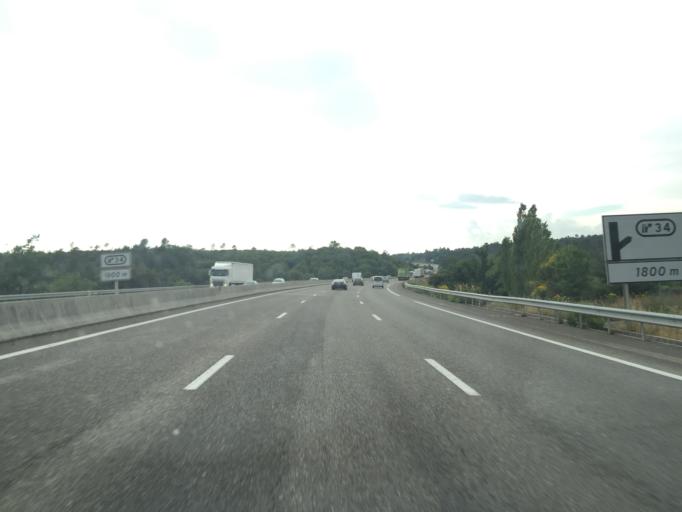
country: FR
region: Provence-Alpes-Cote d'Azur
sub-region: Departement du Var
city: Tourves
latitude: 43.4384
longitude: 5.9083
